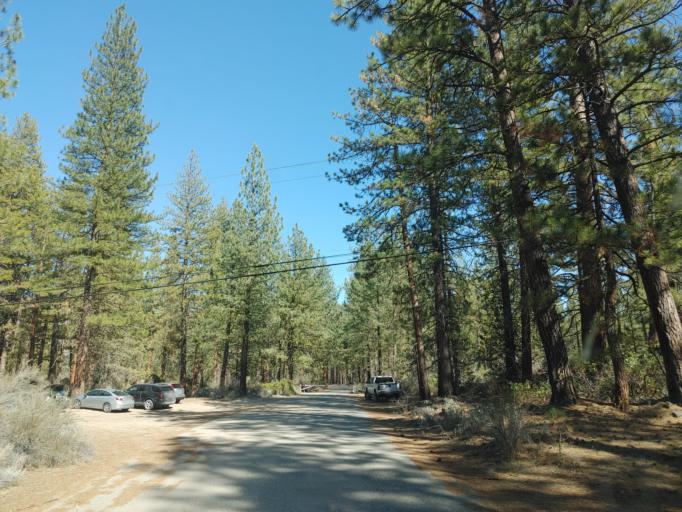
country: US
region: California
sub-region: Shasta County
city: Burney
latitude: 40.6849
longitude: -121.4221
